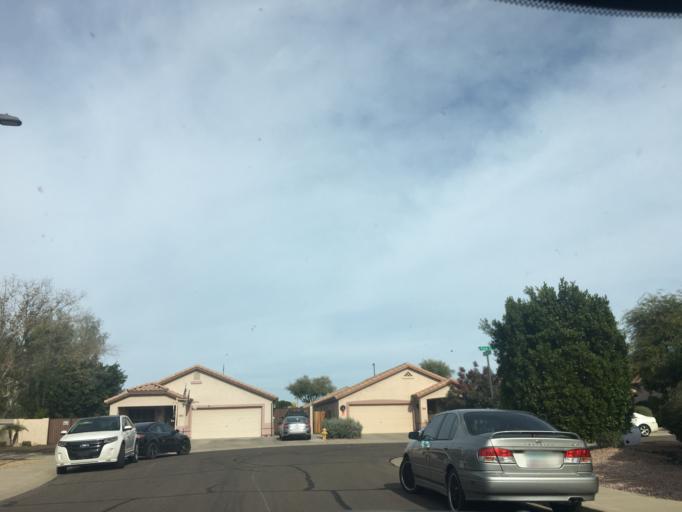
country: US
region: Arizona
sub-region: Maricopa County
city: Gilbert
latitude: 33.3526
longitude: -111.8093
